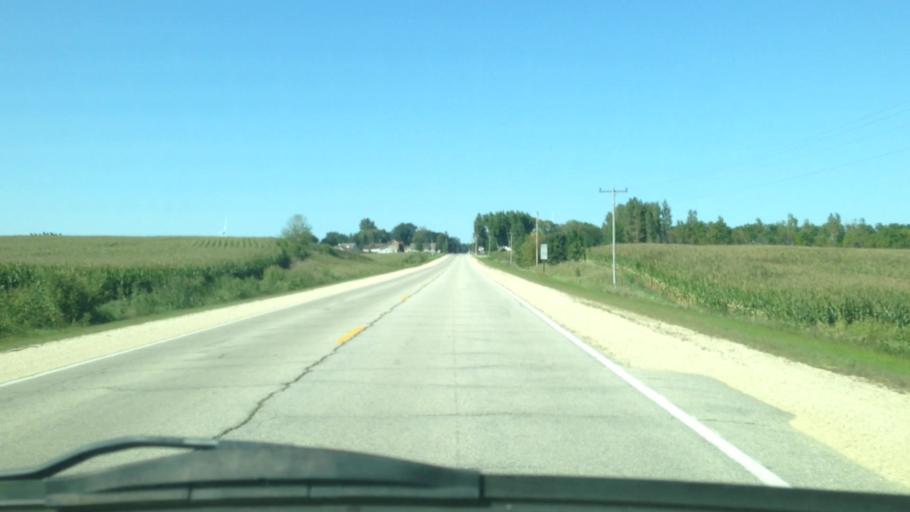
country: US
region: Minnesota
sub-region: Winona County
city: Lewiston
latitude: 43.9714
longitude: -91.8692
